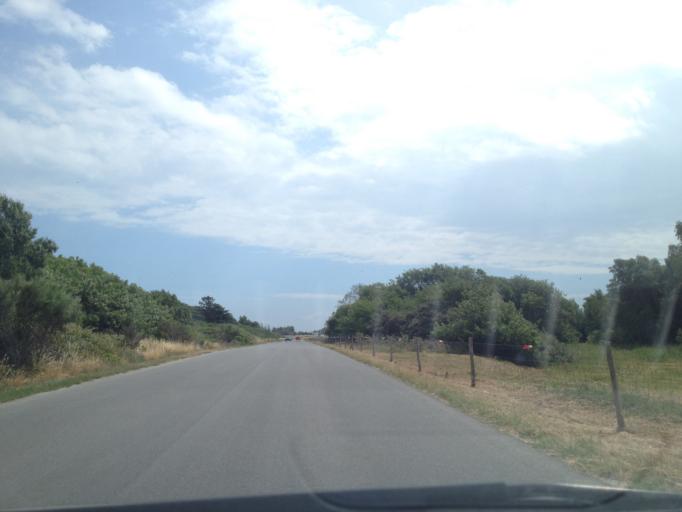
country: DK
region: Central Jutland
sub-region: Syddjurs Kommune
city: Ebeltoft
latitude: 56.1549
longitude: 10.6831
